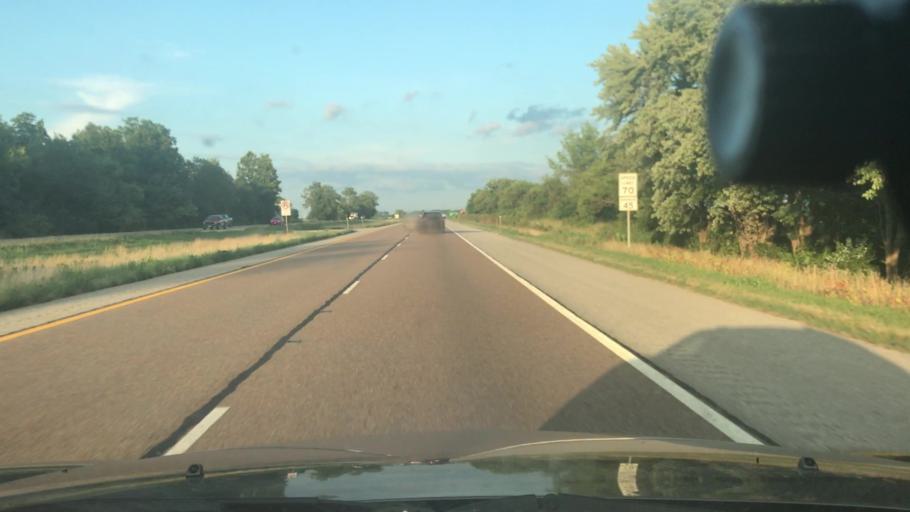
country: US
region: Illinois
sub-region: Saint Clair County
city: Lebanon
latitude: 38.5506
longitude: -89.7953
